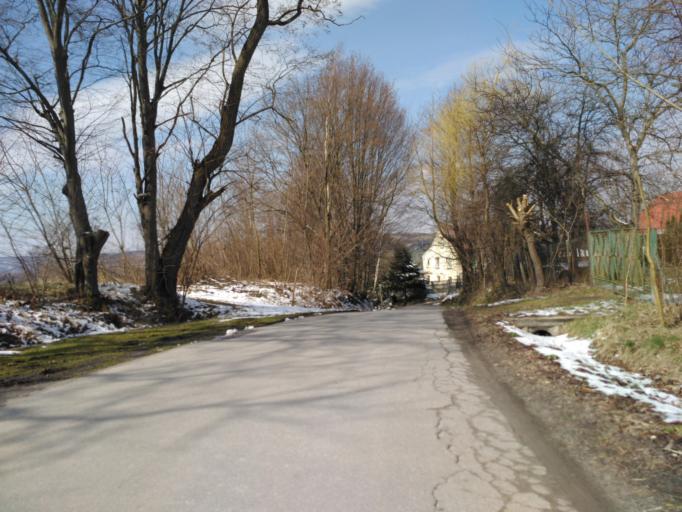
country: PL
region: Subcarpathian Voivodeship
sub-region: Powiat ropczycko-sedziszowski
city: Niedzwiada
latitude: 49.9995
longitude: 21.5679
